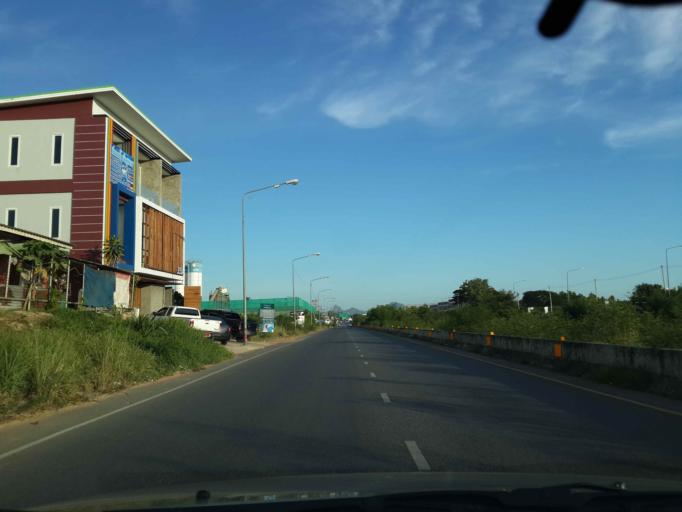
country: TH
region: Chon Buri
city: Phatthaya
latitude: 12.8629
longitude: 100.9127
